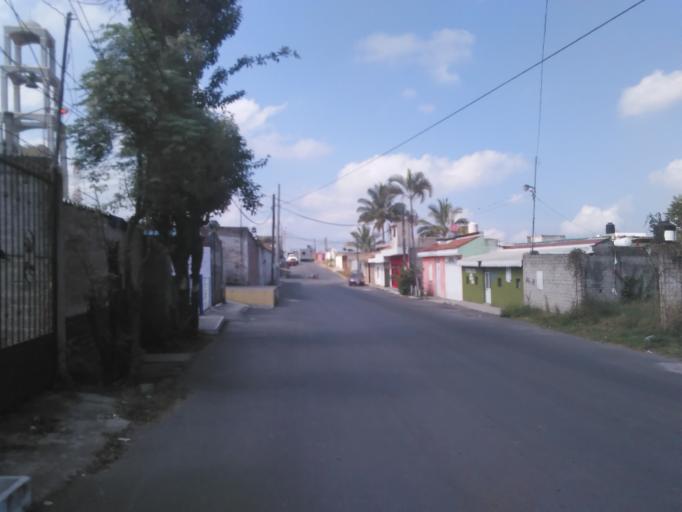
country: MX
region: Nayarit
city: Tepic
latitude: 21.5259
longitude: -104.9231
